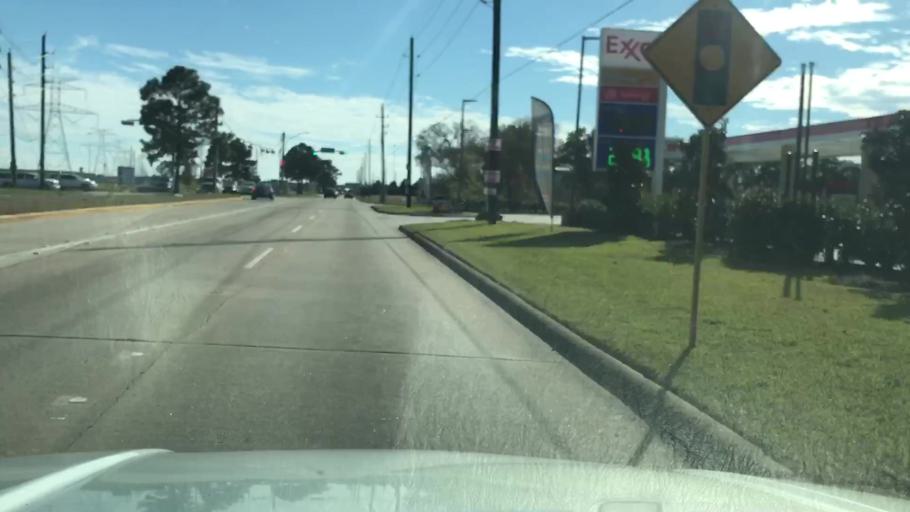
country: US
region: Texas
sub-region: Fort Bend County
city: Cinco Ranch
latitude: 29.7943
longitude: -95.7525
